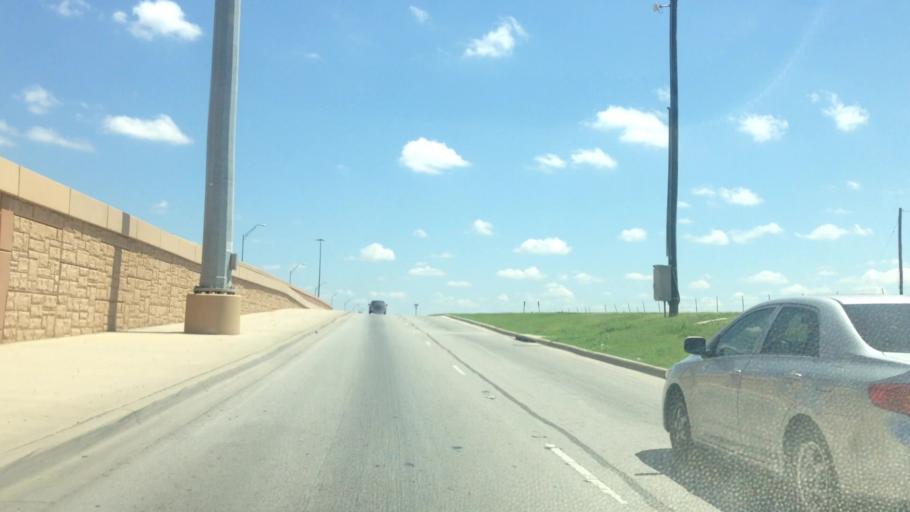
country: US
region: Texas
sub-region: Tarrant County
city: Haltom City
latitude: 32.8308
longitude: -97.2886
